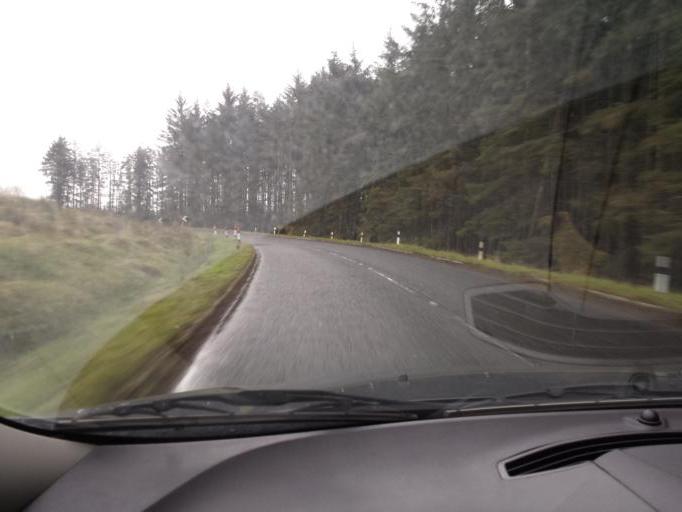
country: GB
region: Northern Ireland
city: Glenariff
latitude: 55.0272
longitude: -6.1420
